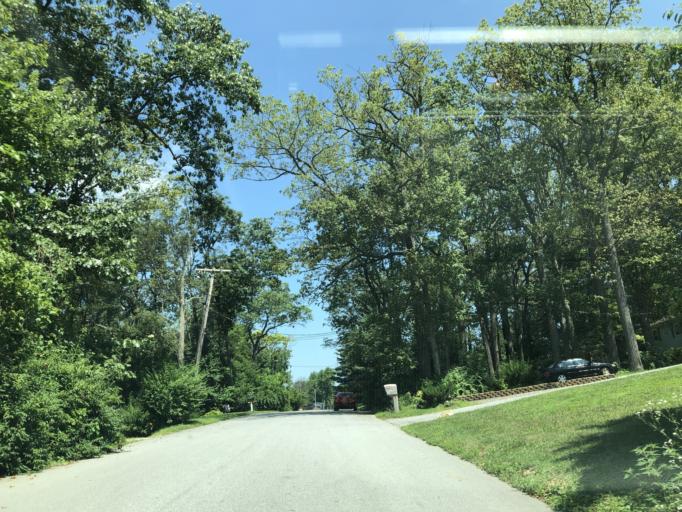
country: US
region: Maryland
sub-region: Carroll County
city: Westminster
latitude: 39.5371
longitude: -76.9857
